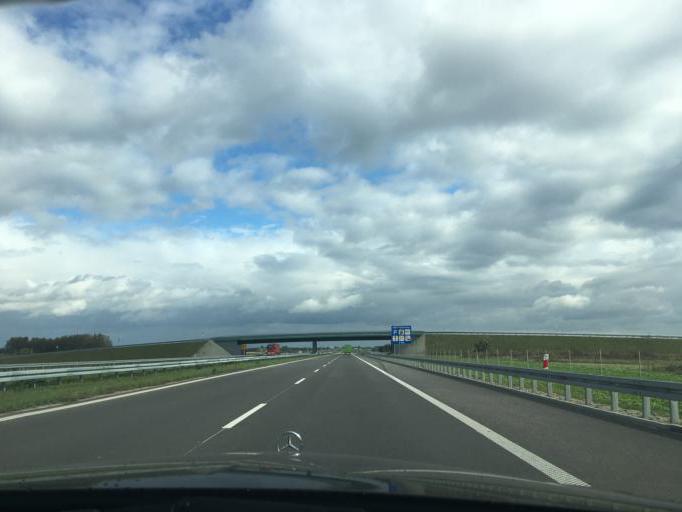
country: PL
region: Subcarpathian Voivodeship
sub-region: Powiat rzeszowski
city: Wolka Podlesna
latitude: 50.0939
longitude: 22.0958
